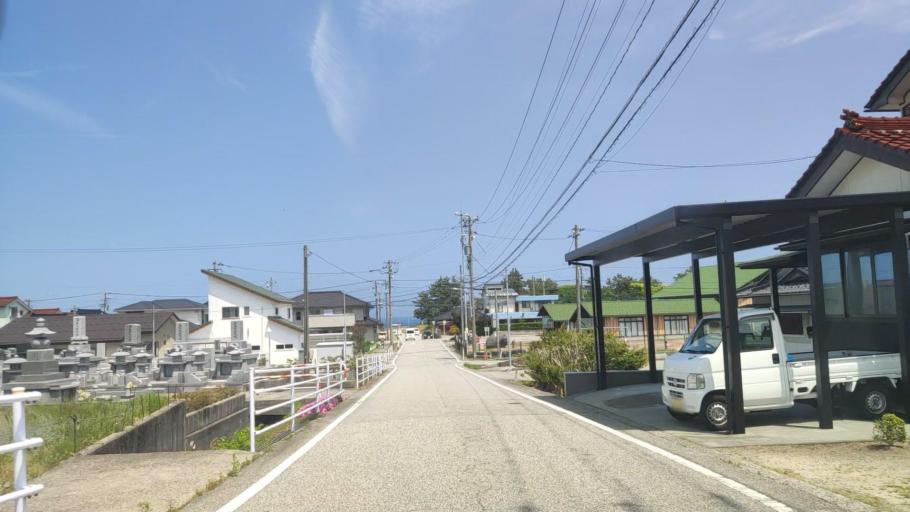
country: JP
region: Toyama
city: Nyuzen
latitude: 36.9723
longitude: 137.5924
